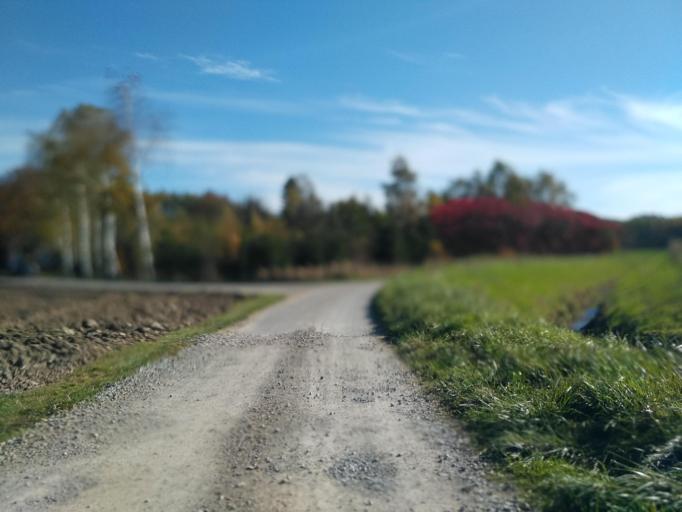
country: PL
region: Subcarpathian Voivodeship
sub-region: Powiat ropczycko-sedziszowski
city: Iwierzyce
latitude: 50.0100
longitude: 21.7593
